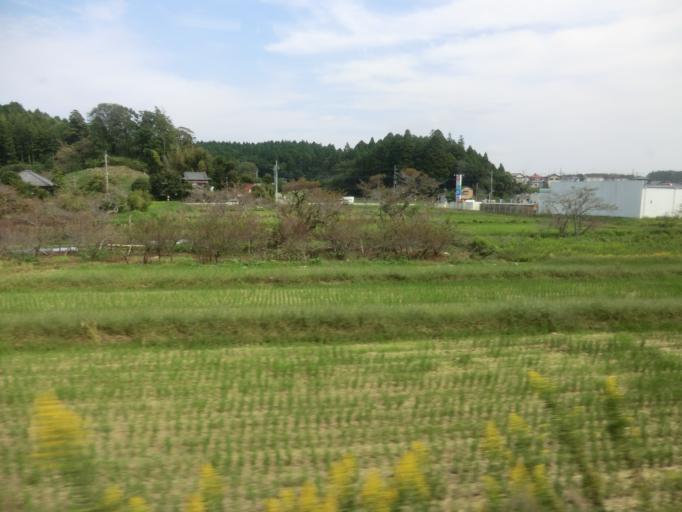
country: JP
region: Chiba
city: Yachimata
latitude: 35.6349
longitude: 140.3534
